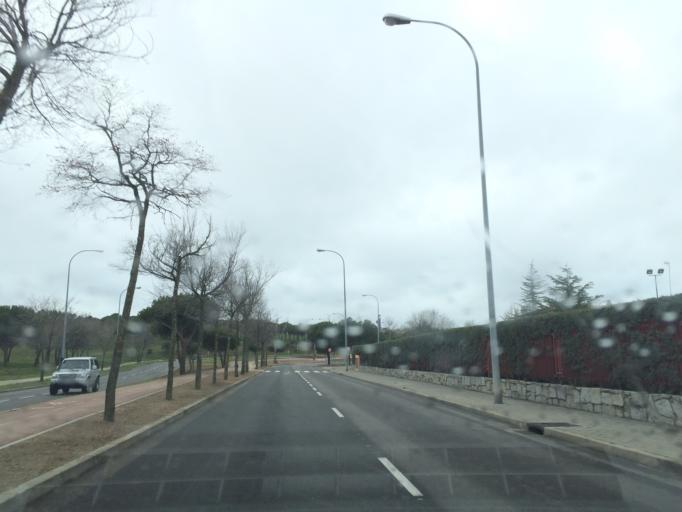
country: ES
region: Madrid
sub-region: Provincia de Madrid
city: Tres Cantos
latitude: 40.5936
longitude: -3.6948
